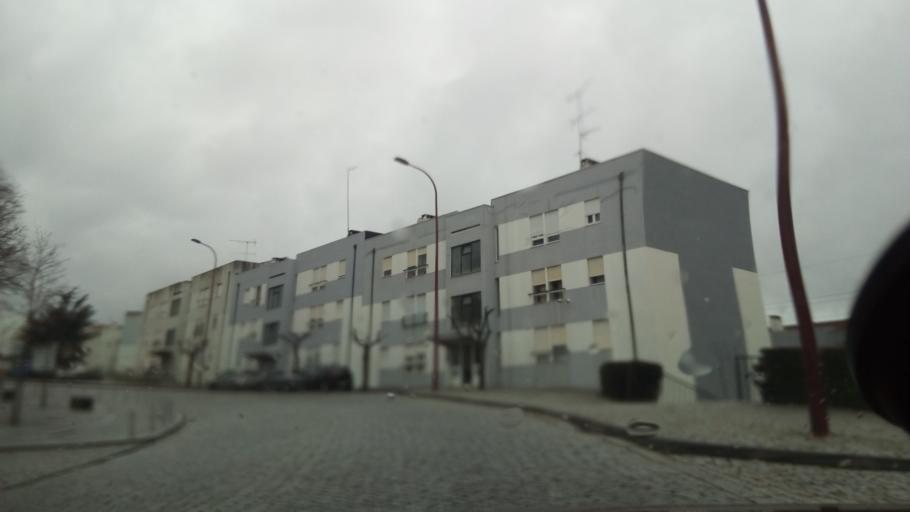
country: PT
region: Guarda
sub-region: Celorico da Beira
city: Celorico da Beira
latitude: 40.6422
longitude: -7.3900
